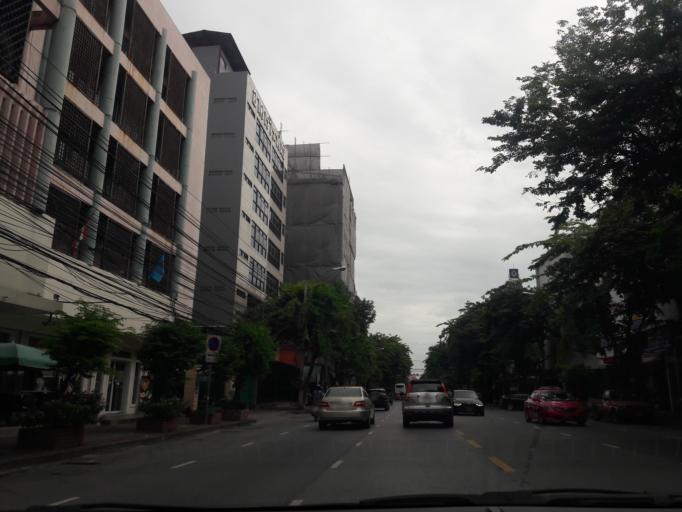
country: TH
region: Bangkok
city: Bangkok
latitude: 13.7505
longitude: 100.5082
